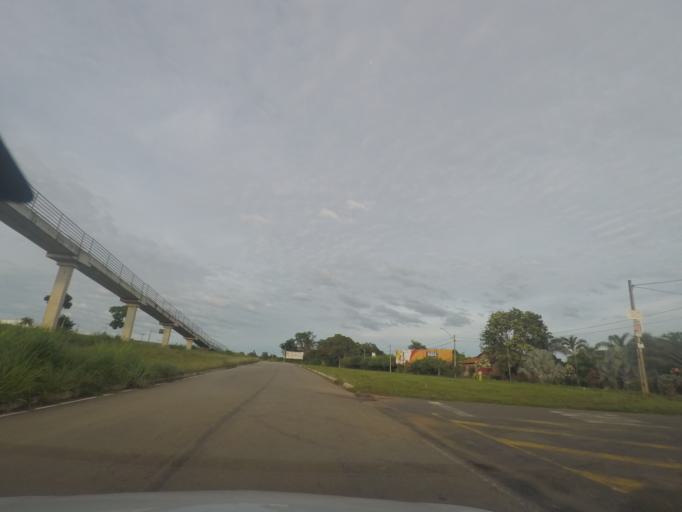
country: BR
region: Goias
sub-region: Trindade
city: Trindade
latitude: -16.7315
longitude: -49.3959
